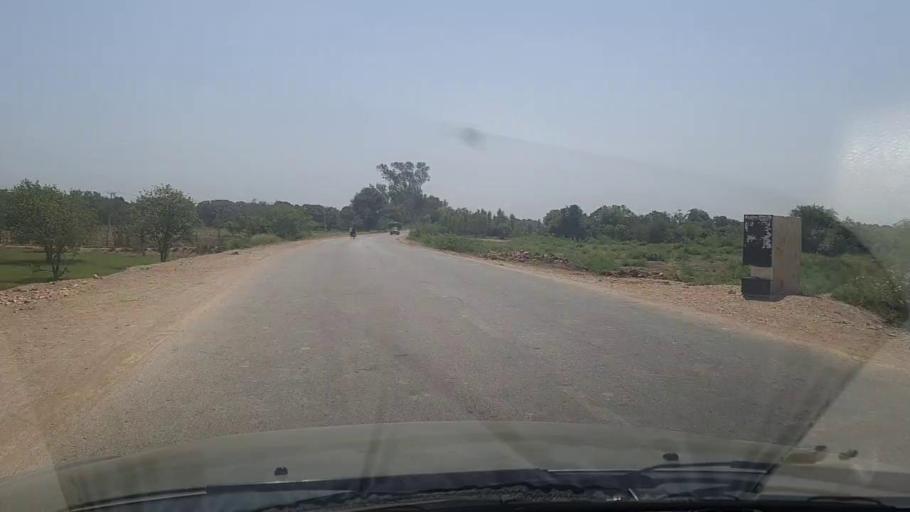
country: PK
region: Sindh
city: Tando Jam
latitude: 25.3536
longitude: 68.5046
